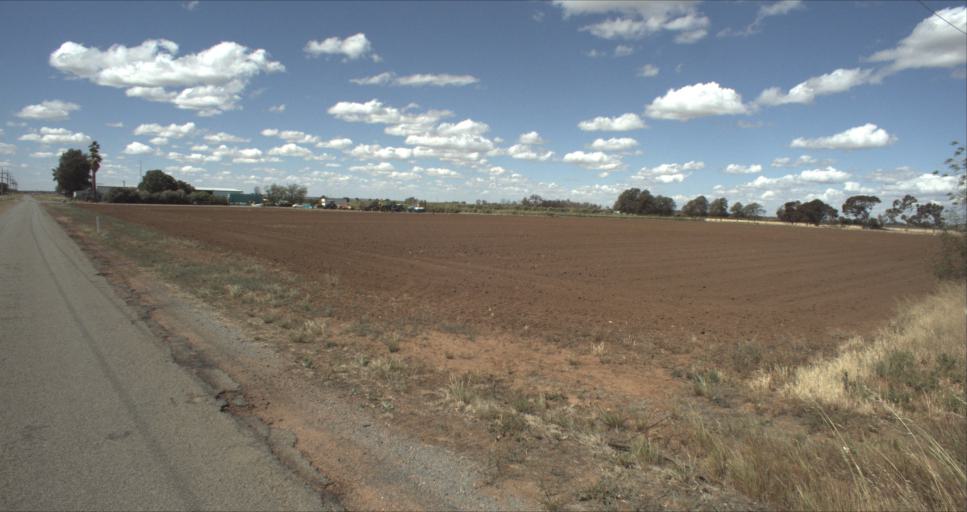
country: AU
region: New South Wales
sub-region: Leeton
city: Leeton
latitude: -34.5134
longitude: 146.2517
